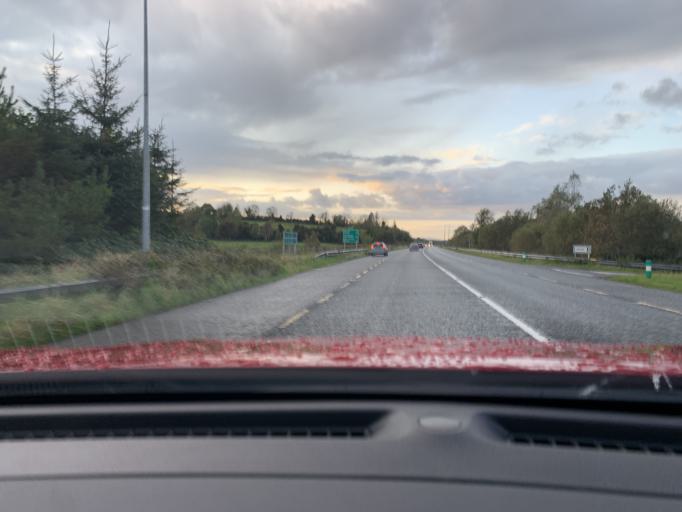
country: IE
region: Connaught
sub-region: County Leitrim
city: Carrick-on-Shannon
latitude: 53.9451
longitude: -8.1174
